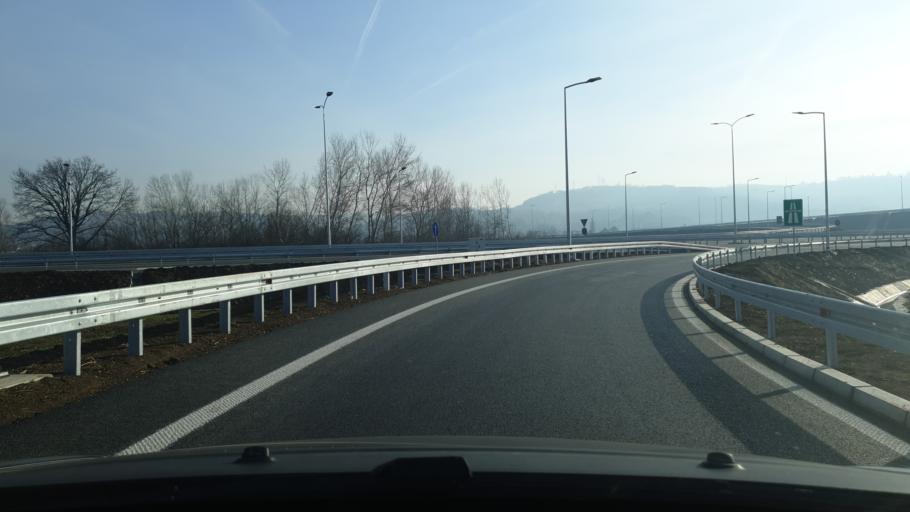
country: RS
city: Baric
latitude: 44.6536
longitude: 20.2325
